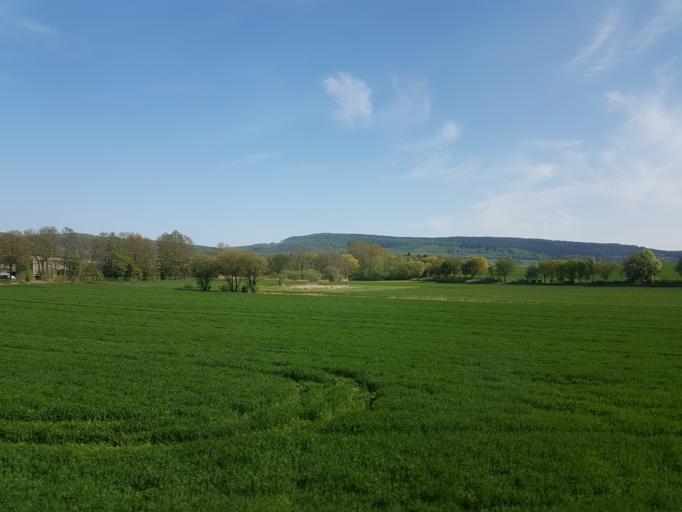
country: DE
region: Lower Saxony
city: Springe
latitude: 52.1941
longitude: 9.5166
